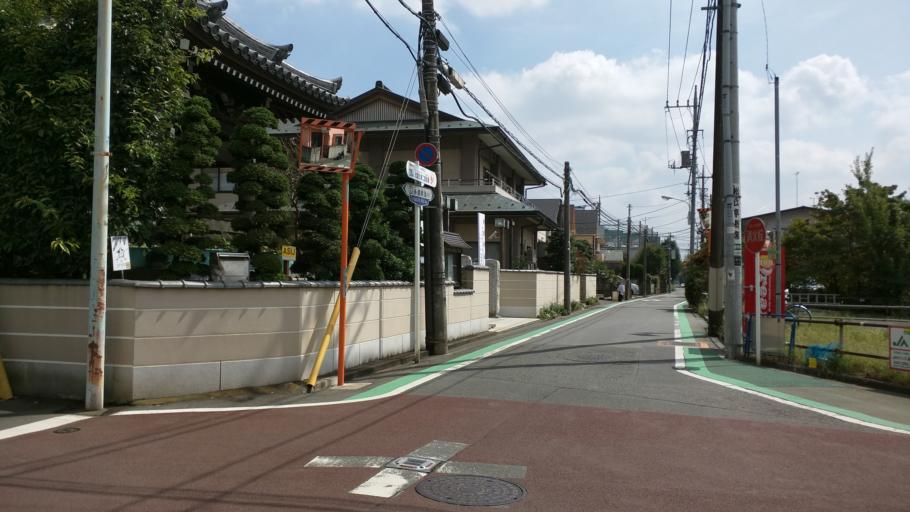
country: JP
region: Tokyo
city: Chofugaoka
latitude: 35.6808
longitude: 139.5192
